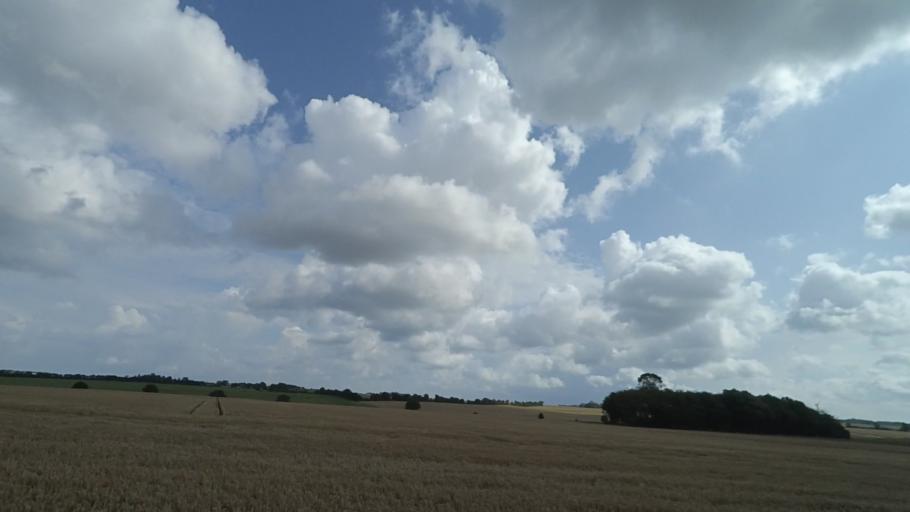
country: DK
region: Central Jutland
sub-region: Norddjurs Kommune
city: Auning
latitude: 56.4948
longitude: 10.4422
